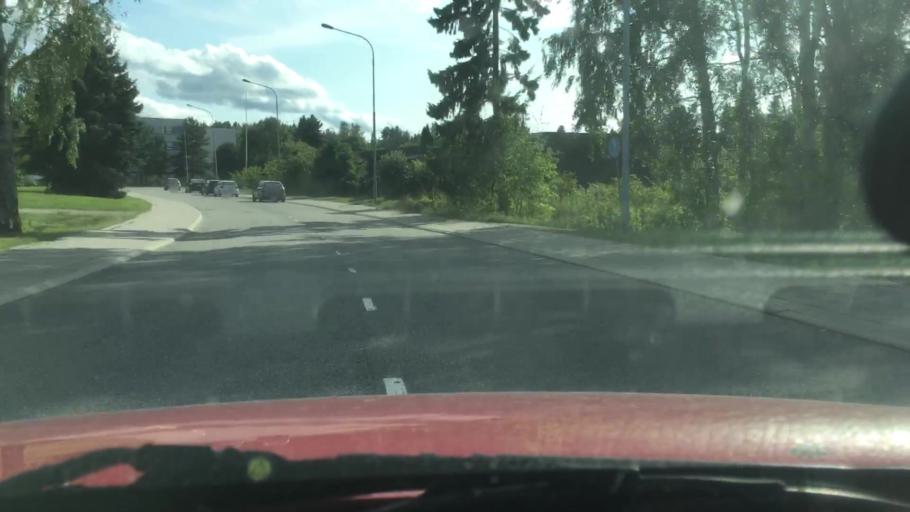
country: FI
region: Varsinais-Suomi
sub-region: Turku
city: Raisio
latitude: 60.4679
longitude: 22.2171
